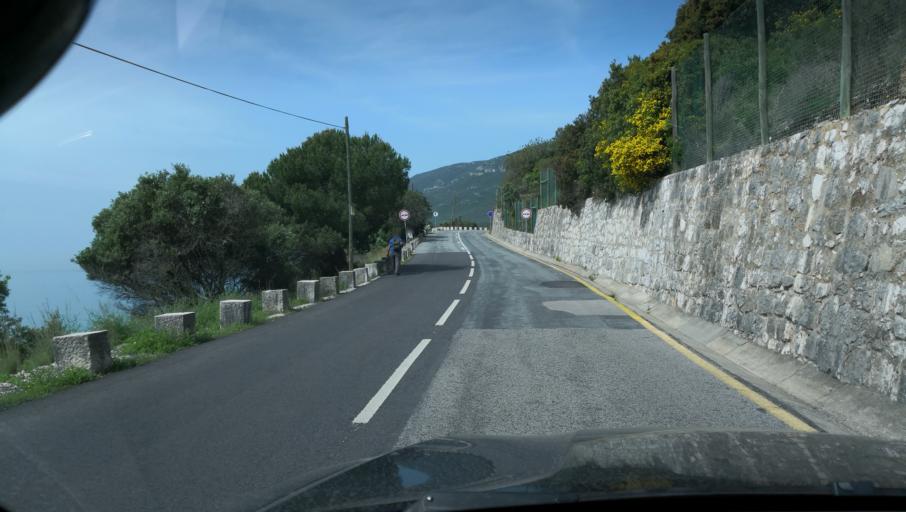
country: PT
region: Setubal
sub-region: Setubal
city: Setubal
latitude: 38.4851
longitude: -8.9606
